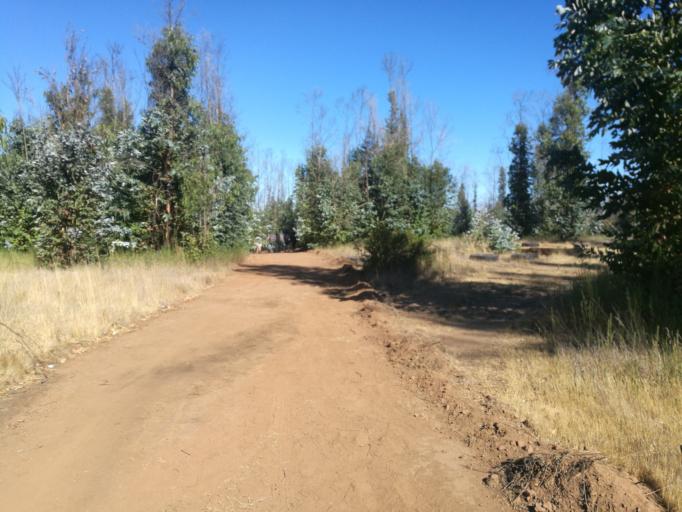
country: CL
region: Valparaiso
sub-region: Provincia de Valparaiso
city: Valparaiso
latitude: -33.0704
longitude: -71.6497
